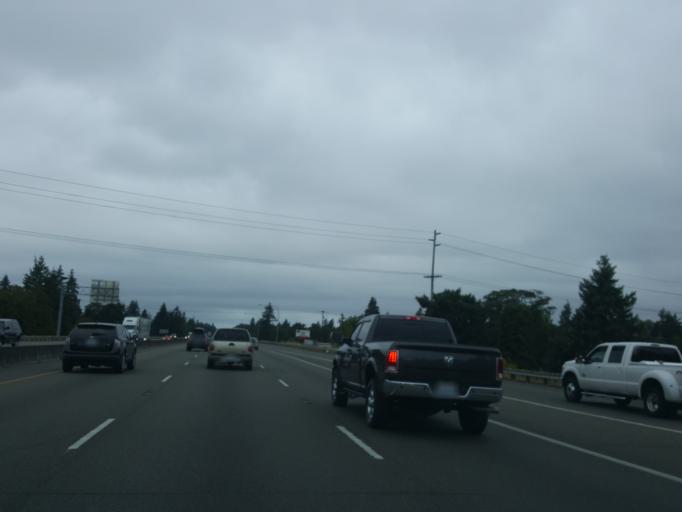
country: US
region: Washington
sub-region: Pierce County
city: Parkland
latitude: 47.1583
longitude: -122.4379
